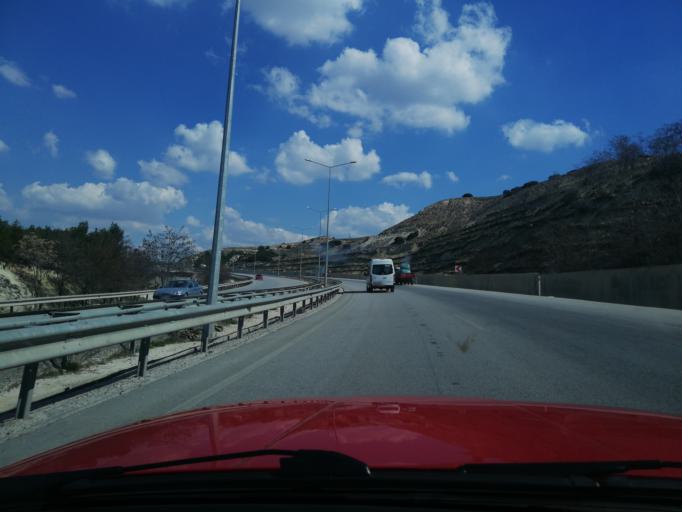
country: TR
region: Burdur
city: Burdur
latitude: 37.7015
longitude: 30.3086
